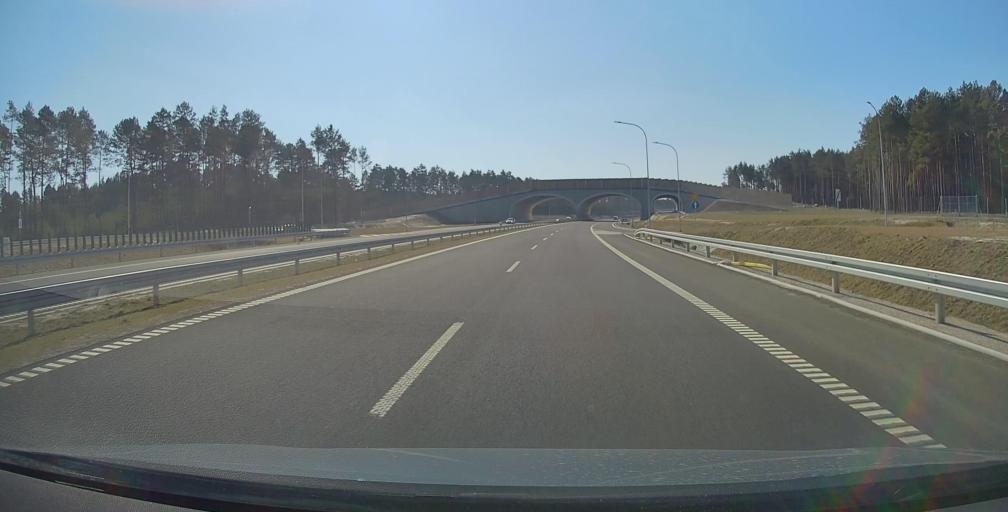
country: PL
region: Subcarpathian Voivodeship
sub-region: Powiat nizanski
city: Jarocin
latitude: 50.6103
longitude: 22.2904
